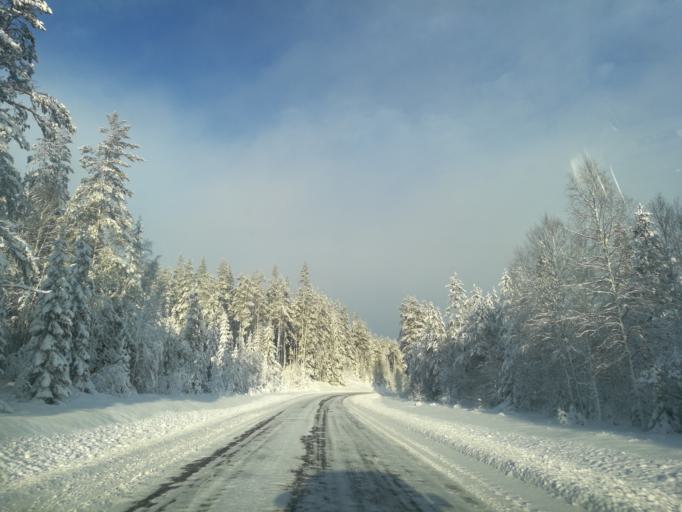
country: SE
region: Vaermland
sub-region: Torsby Kommun
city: Torsby
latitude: 60.5864
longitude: 12.7374
